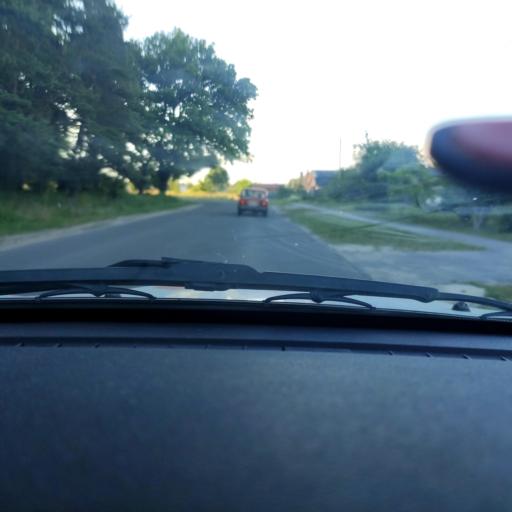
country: RU
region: Voronezj
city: Ramon'
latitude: 51.8995
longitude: 39.2865
